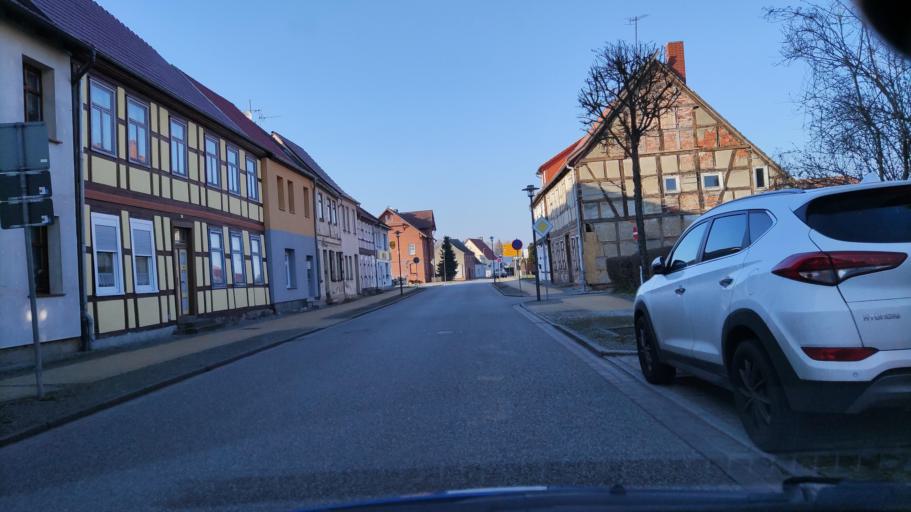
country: DE
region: Saxony-Anhalt
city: Seehausen
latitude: 52.8930
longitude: 11.7534
